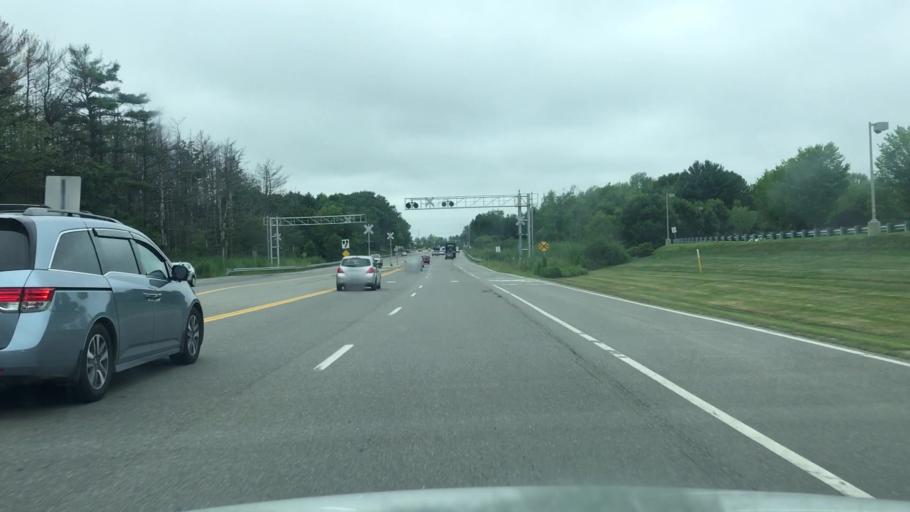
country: US
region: New Hampshire
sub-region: Rockingham County
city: Greenland
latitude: 43.0487
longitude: -70.8163
